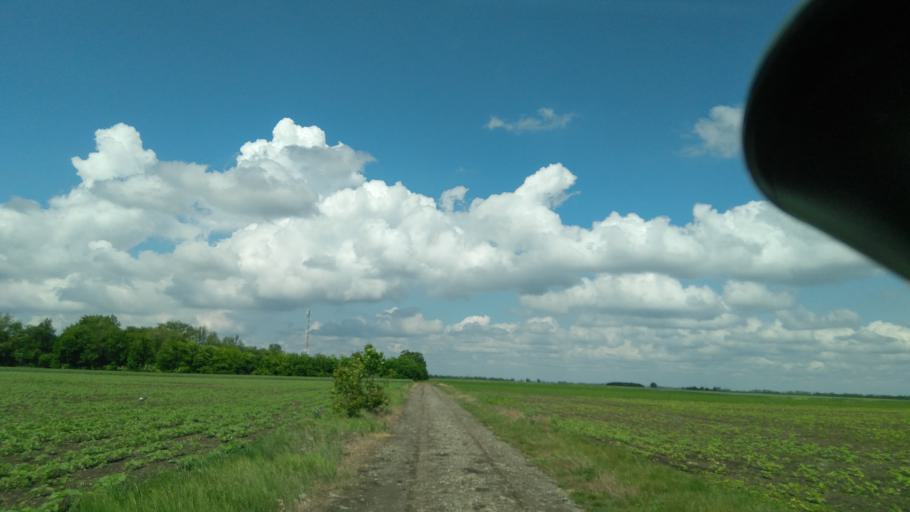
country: HU
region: Bekes
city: Mezobereny
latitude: 46.8338
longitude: 21.0121
